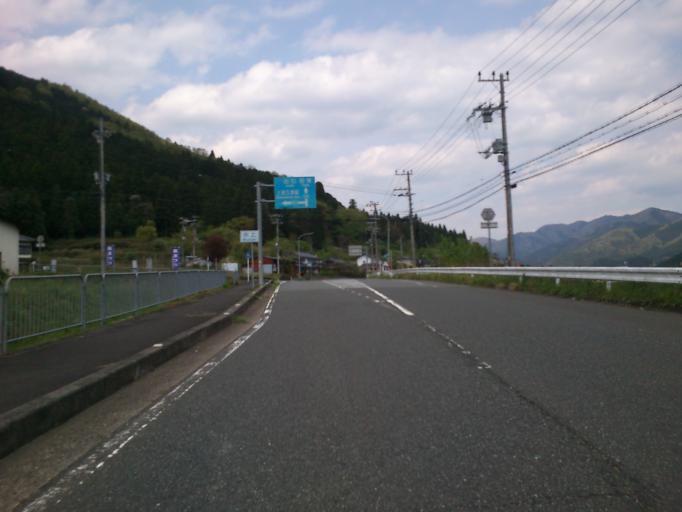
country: JP
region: Kyoto
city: Fukuchiyama
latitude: 35.3433
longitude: 134.9380
